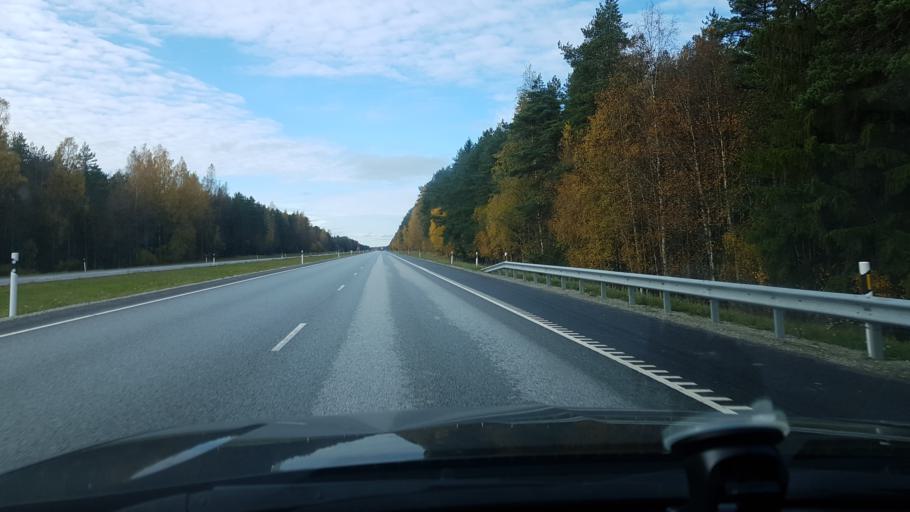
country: EE
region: Harju
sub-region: Loksa linn
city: Loksa
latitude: 59.4631
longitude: 25.6695
